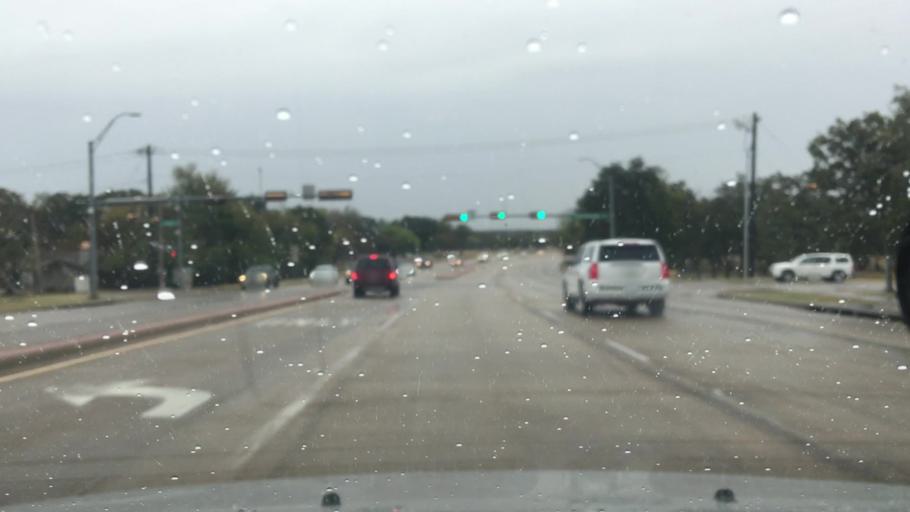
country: US
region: Texas
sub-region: Denton County
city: Denton
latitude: 33.2356
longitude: -97.1073
